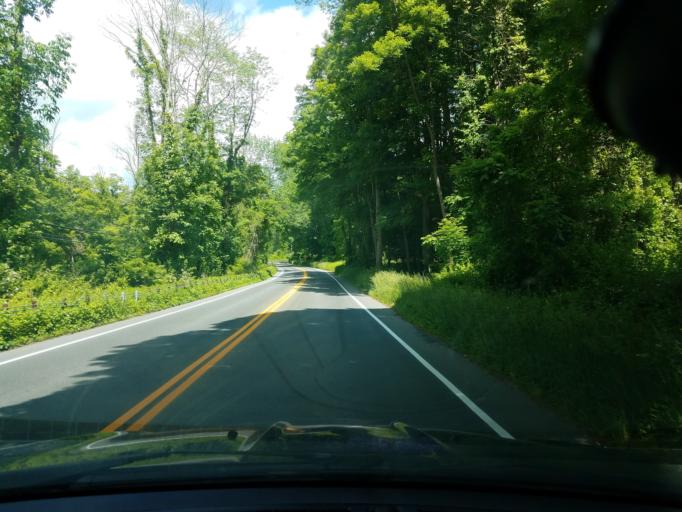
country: US
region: Connecticut
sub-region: Fairfield County
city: Georgetown
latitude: 41.2975
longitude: -73.3981
